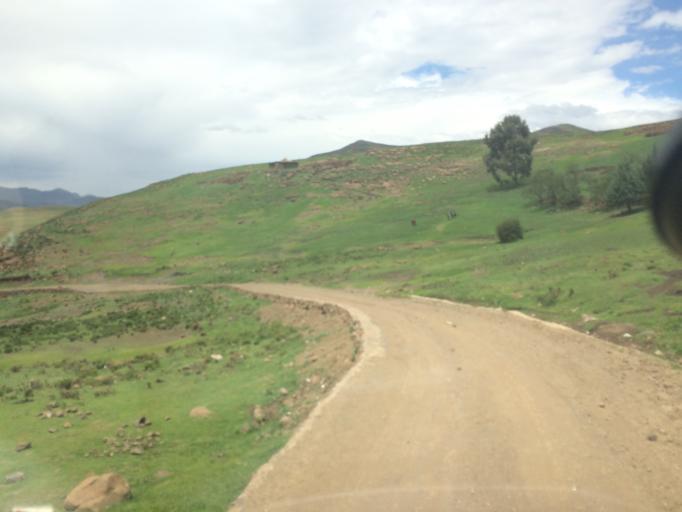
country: LS
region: Maseru
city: Nako
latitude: -29.8546
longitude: 28.0312
